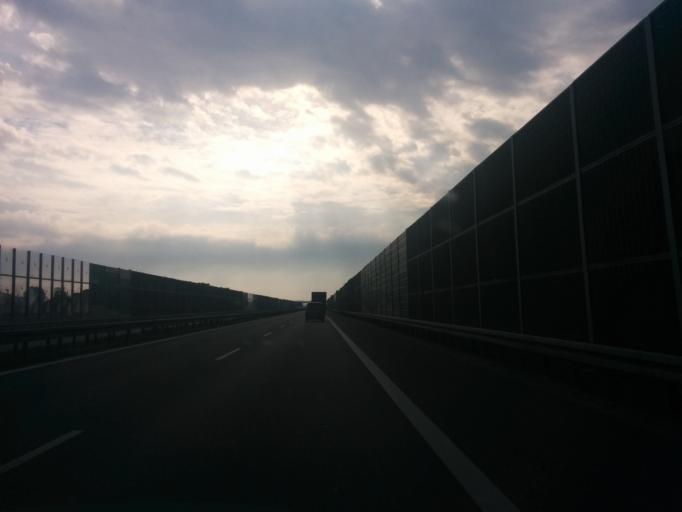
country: PL
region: Masovian Voivodeship
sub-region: Powiat bialobrzeski
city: Stara Blotnica
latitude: 51.5488
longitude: 21.0469
